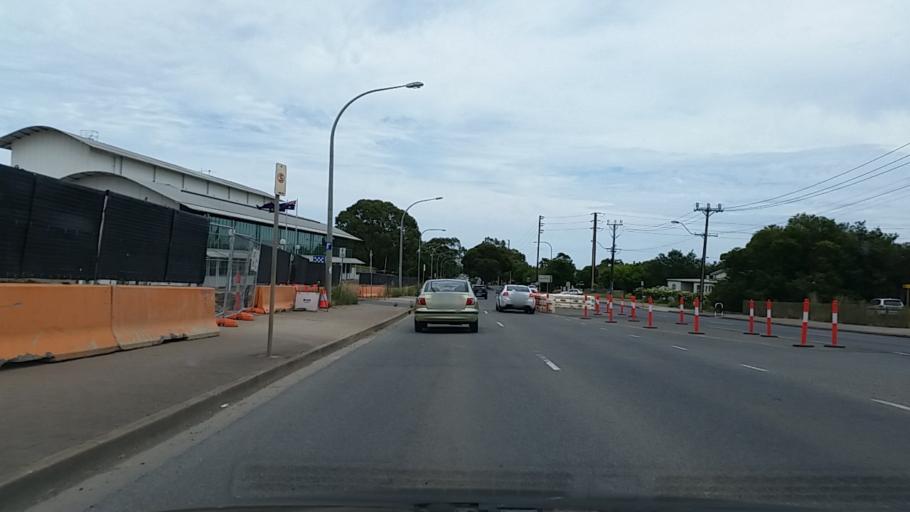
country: AU
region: South Australia
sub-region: Marion
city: Marion
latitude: -35.0168
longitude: 138.5659
